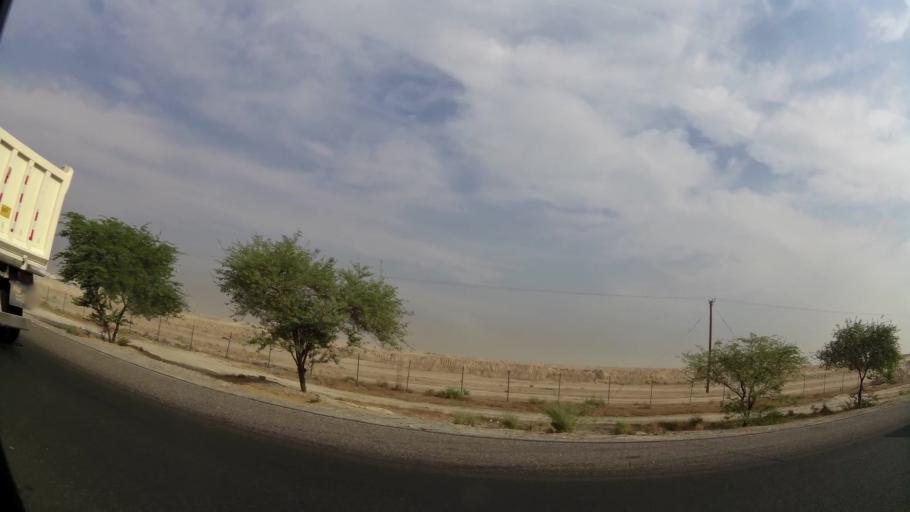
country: KW
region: Muhafazat al Jahra'
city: Al Jahra'
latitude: 29.2910
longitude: 47.7595
